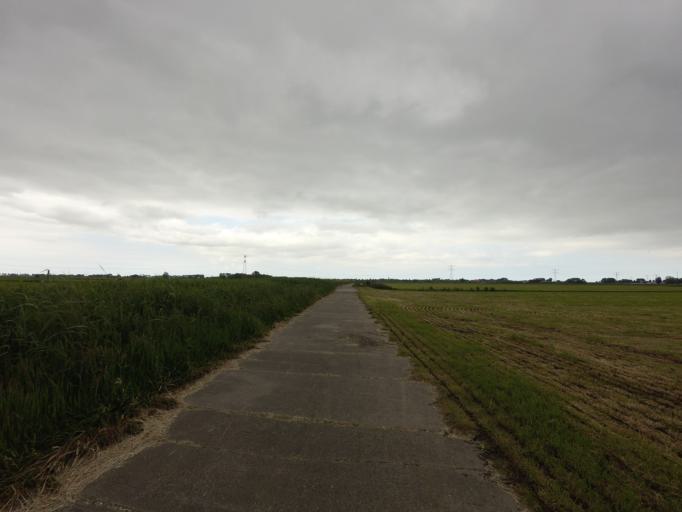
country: NL
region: North Holland
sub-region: Gemeente Hoorn
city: Hoorn
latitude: 52.6598
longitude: 5.0236
